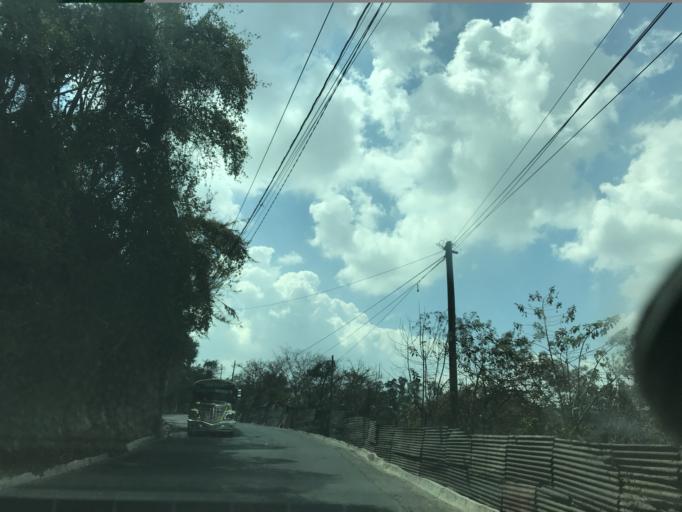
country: GT
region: Guatemala
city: Mixco
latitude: 14.6742
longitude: -90.5732
